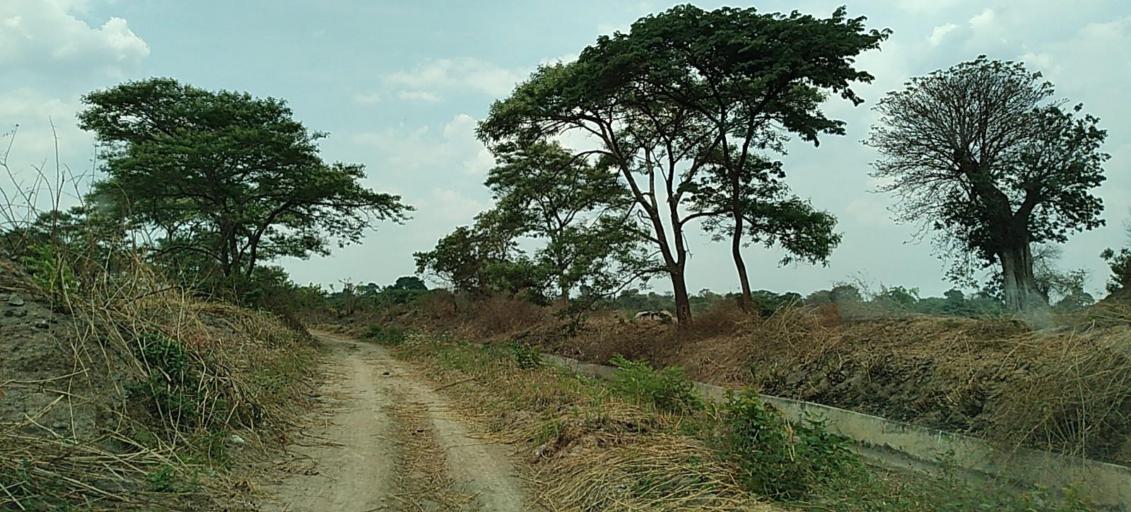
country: ZM
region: Copperbelt
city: Chililabombwe
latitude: -12.3575
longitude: 27.8044
